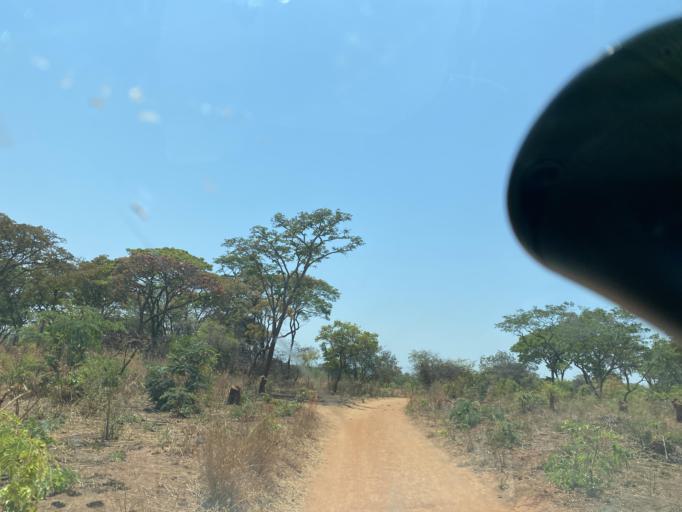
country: ZM
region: Lusaka
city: Chongwe
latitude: -15.4229
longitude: 29.1787
